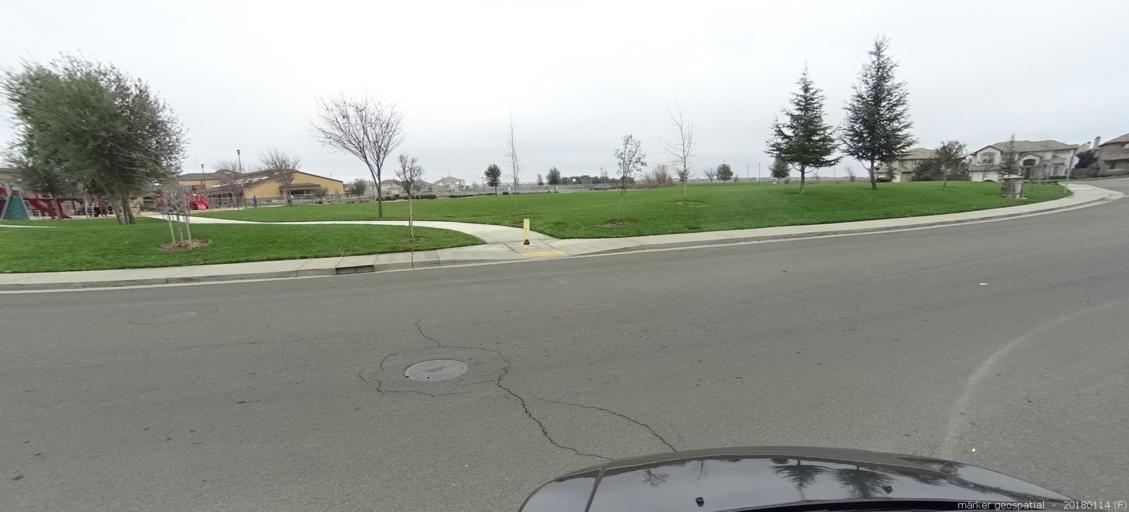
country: US
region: California
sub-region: Sacramento County
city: Rancho Cordova
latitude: 38.5451
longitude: -121.2356
